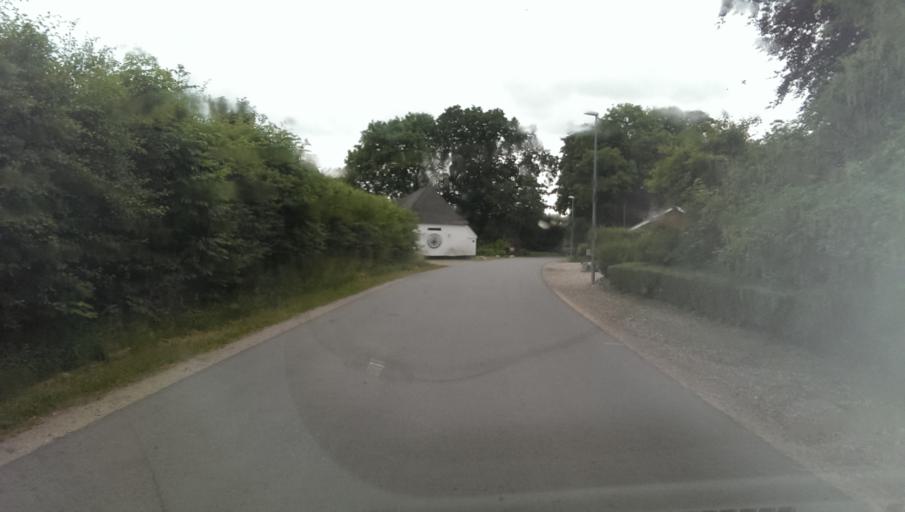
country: DK
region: South Denmark
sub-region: Esbjerg Kommune
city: Bramming
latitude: 55.4337
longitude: 8.7181
